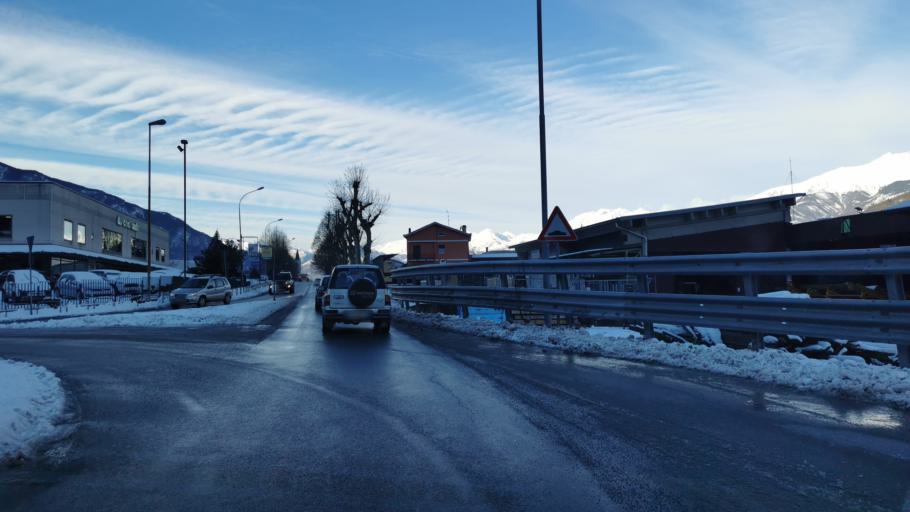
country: IT
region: Lombardy
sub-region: Provincia di Sondrio
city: Andalo Valtellino
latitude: 46.1376
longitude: 9.4733
